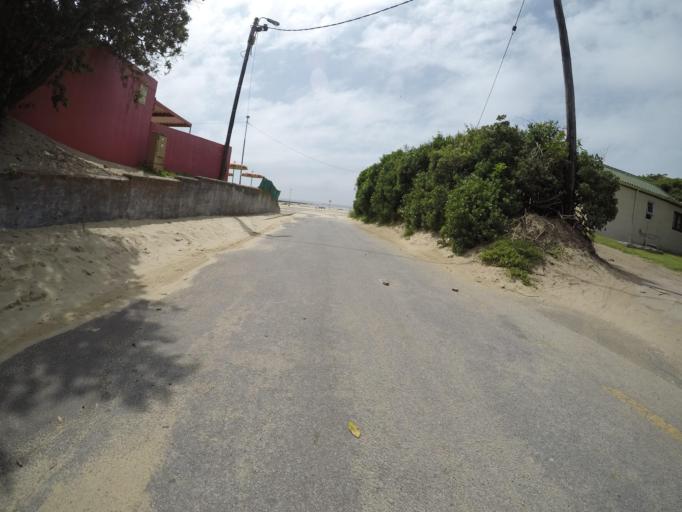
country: ZA
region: Eastern Cape
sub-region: Buffalo City Metropolitan Municipality
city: East London
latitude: -32.9340
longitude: 28.0305
